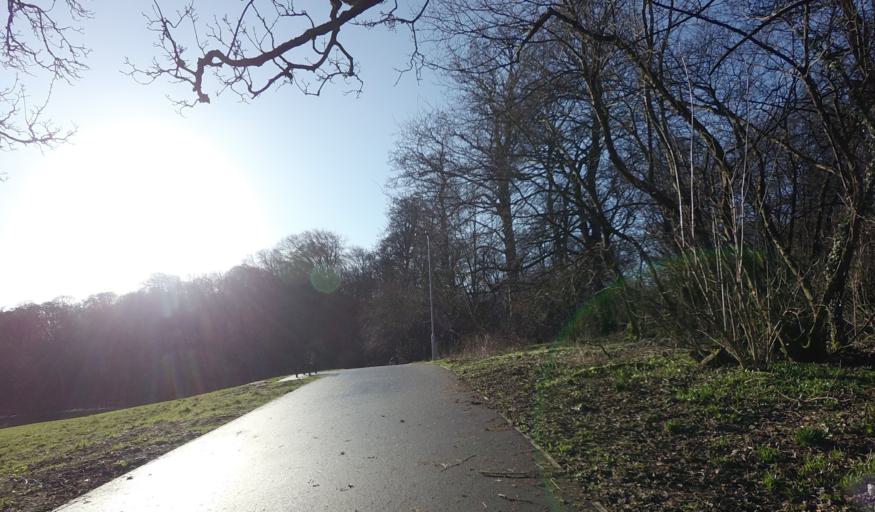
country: GB
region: Scotland
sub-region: Edinburgh
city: Colinton
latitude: 55.9640
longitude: -3.2802
